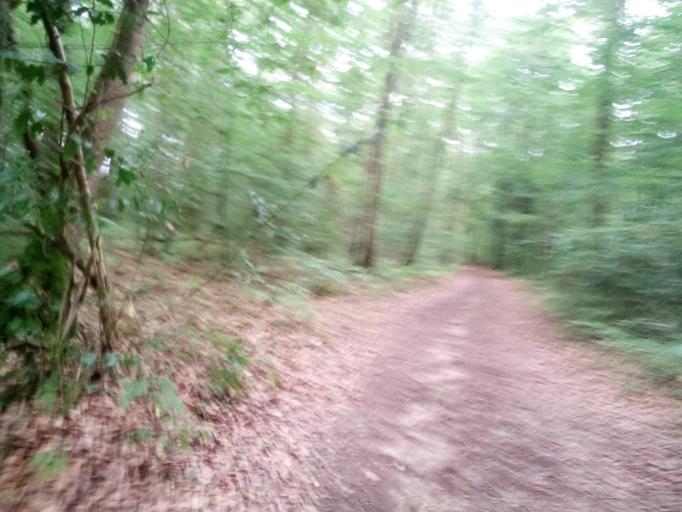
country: FR
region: Lower Normandy
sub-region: Departement du Calvados
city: Clinchamps-sur-Orne
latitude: 49.0464
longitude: -0.4370
